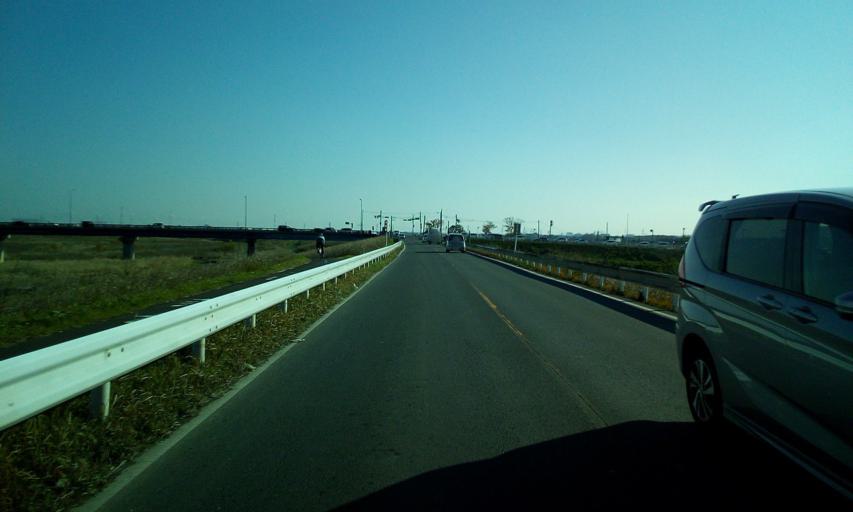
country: JP
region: Chiba
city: Noda
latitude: 35.9395
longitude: 139.8436
